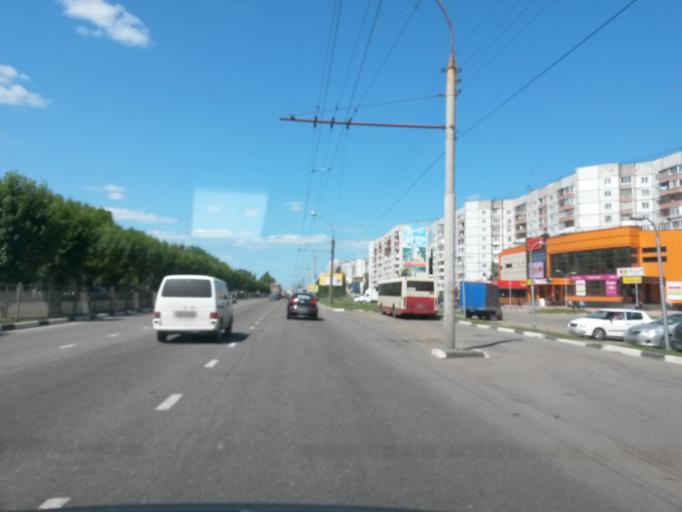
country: RU
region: Jaroslavl
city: Yaroslavl
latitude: 57.6932
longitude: 39.7725
